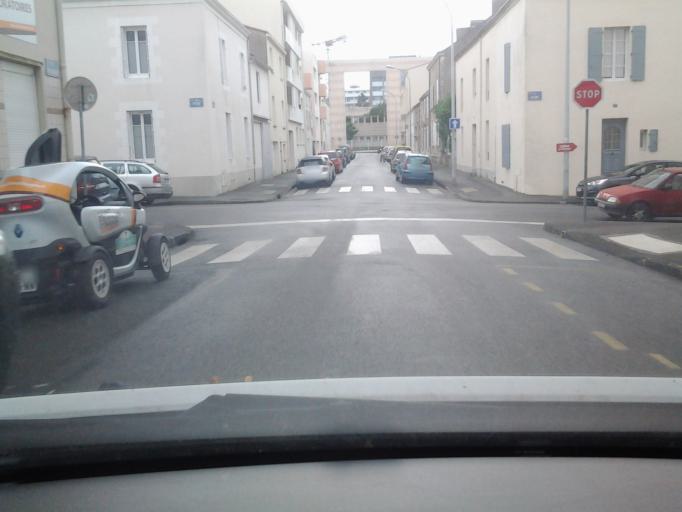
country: FR
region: Pays de la Loire
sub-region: Departement de la Vendee
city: La Roche-sur-Yon
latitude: 46.6733
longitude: -1.4268
